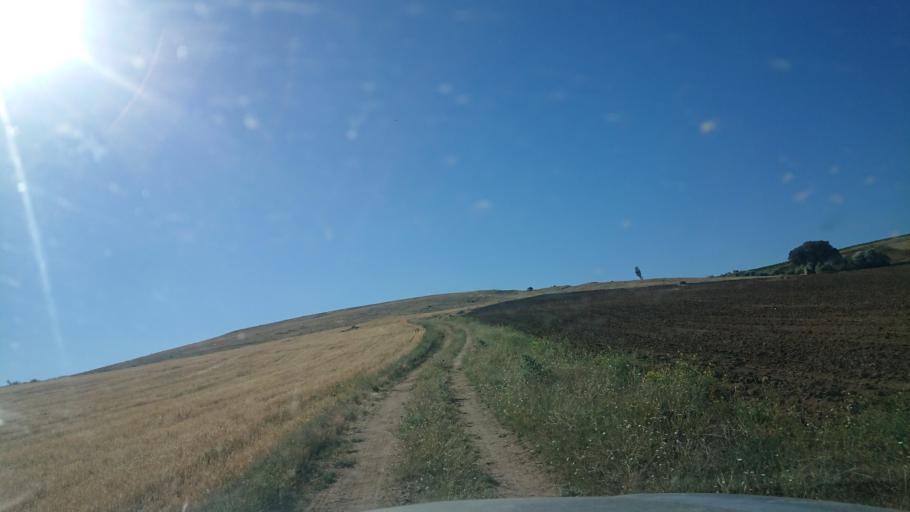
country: TR
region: Aksaray
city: Agacoren
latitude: 38.8393
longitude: 33.9346
